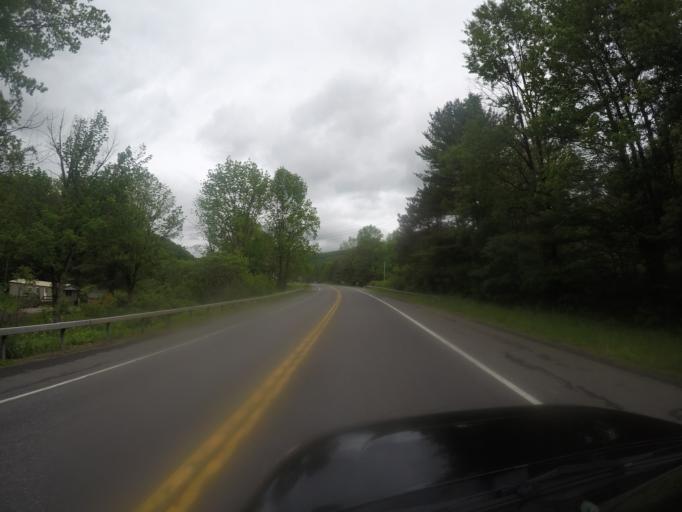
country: US
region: New York
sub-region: Ulster County
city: Shokan
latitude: 42.1105
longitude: -74.3551
